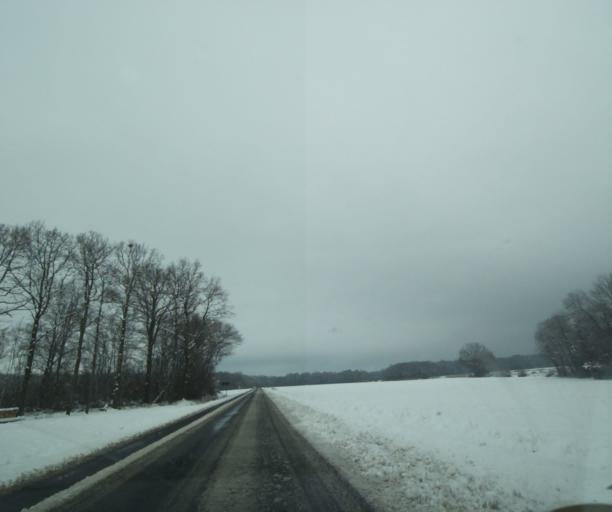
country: FR
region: Champagne-Ardenne
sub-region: Departement de la Haute-Marne
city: Montier-en-Der
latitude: 48.5088
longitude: 4.7480
